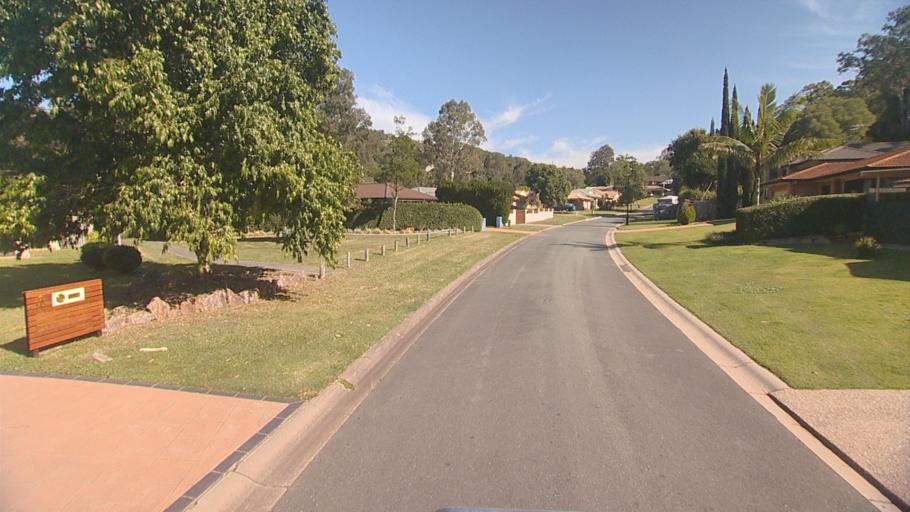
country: AU
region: Queensland
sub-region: Logan
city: Windaroo
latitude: -27.7406
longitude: 153.1838
